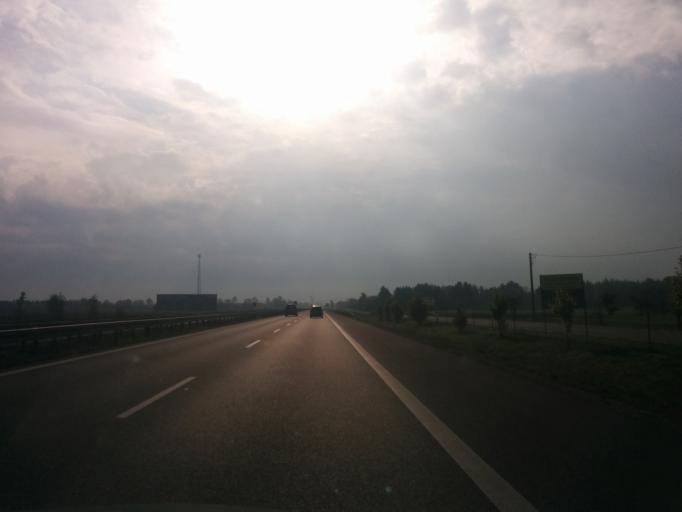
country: PL
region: Masovian Voivodeship
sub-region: Powiat radomski
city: Jedlinsk
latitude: 51.5267
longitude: 21.0916
